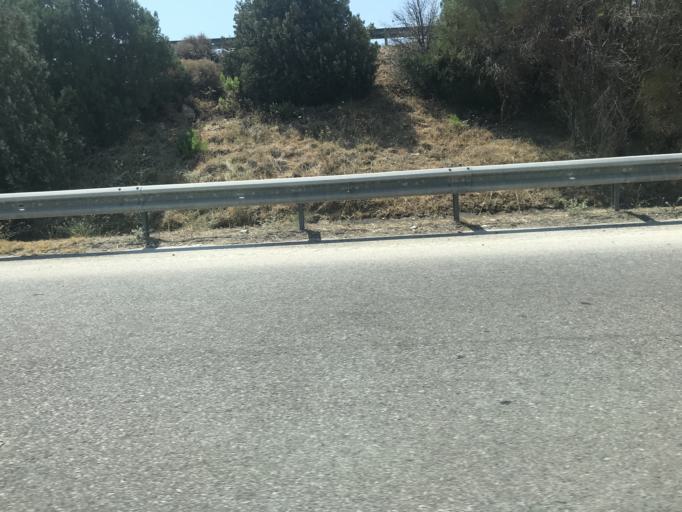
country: TR
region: Izmir
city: Urla
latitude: 38.3186
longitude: 26.7855
